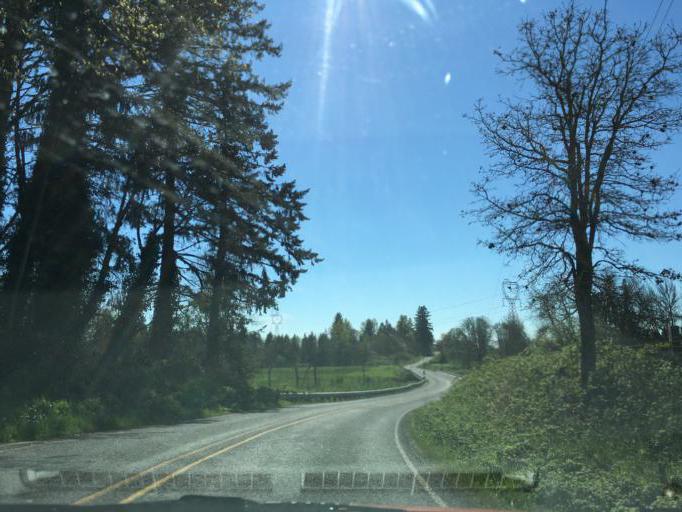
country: US
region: Oregon
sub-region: Marion County
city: Hubbard
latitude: 45.1534
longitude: -122.7227
